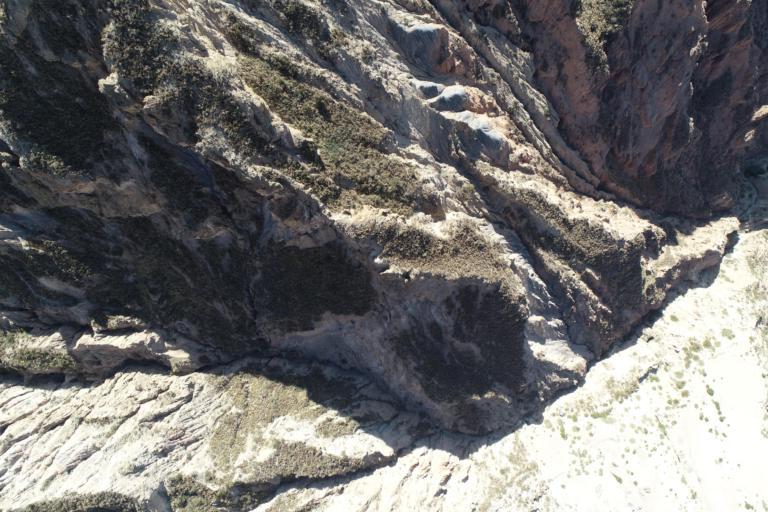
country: BO
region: La Paz
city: La Paz
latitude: -16.5538
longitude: -68.1052
